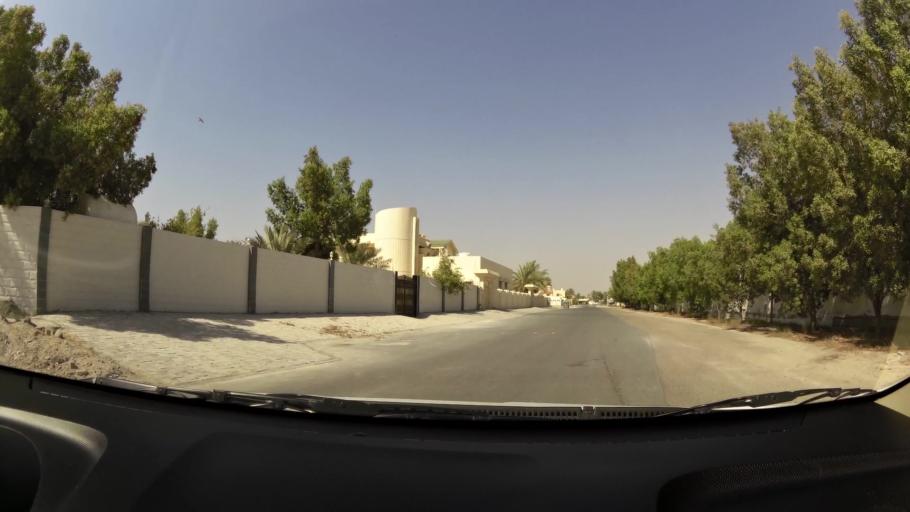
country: AE
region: Ajman
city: Ajman
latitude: 25.4174
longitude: 55.4684
